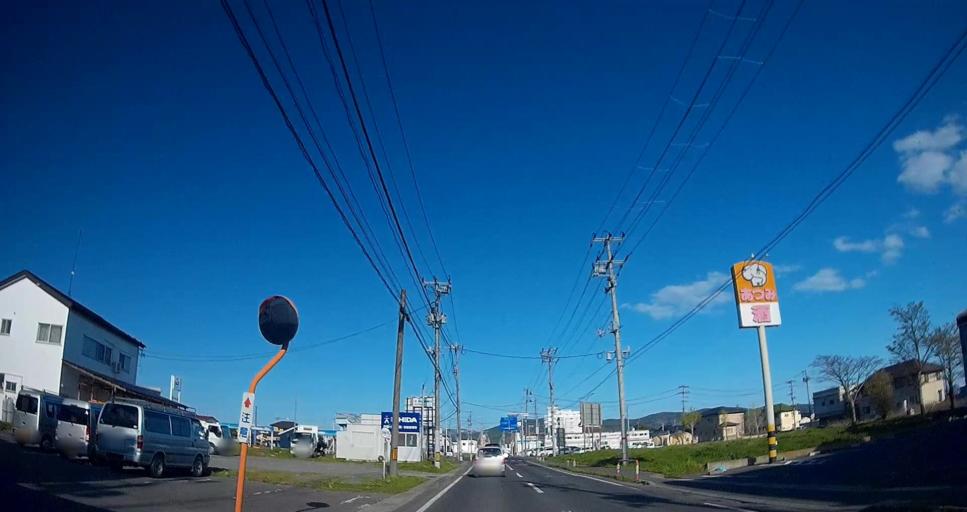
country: JP
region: Miyagi
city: Ishinomaki
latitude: 38.4194
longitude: 141.3341
